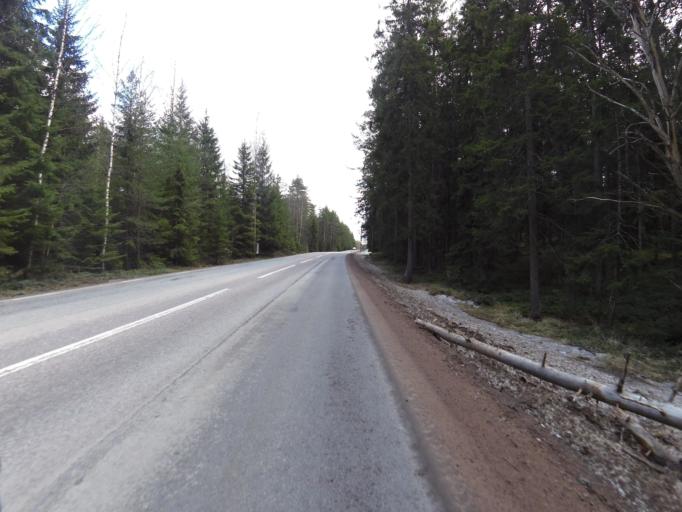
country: SE
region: Dalarna
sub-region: Hedemora Kommun
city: Brunna
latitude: 60.3164
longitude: 16.1379
